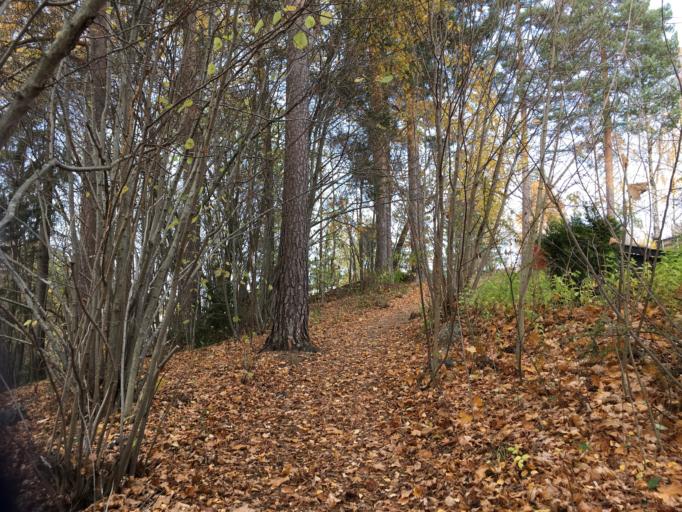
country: NO
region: Akershus
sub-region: Baerum
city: Lysaker
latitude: 59.9363
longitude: 10.6360
